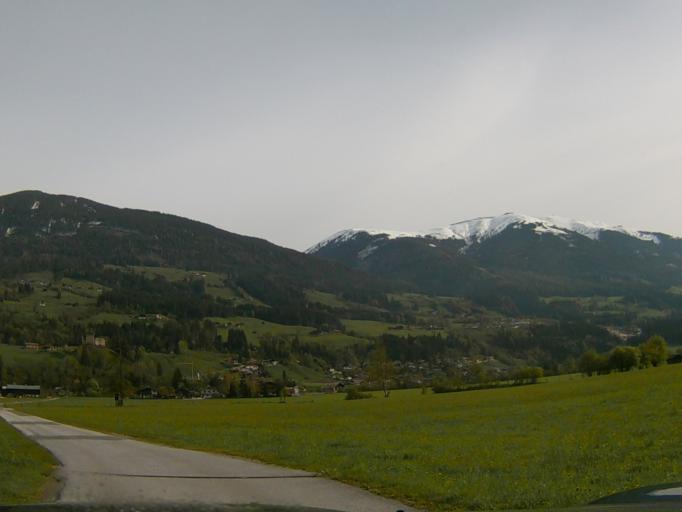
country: AT
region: Salzburg
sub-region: Politischer Bezirk Zell am See
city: Wald im Pinzgau
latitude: 47.2388
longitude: 12.2458
